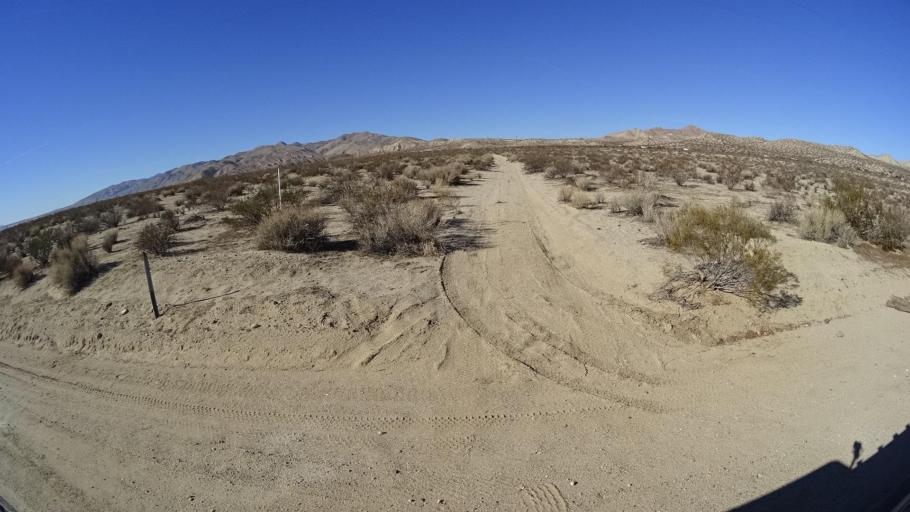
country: US
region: California
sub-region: Kern County
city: California City
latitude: 35.3085
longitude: -117.9860
